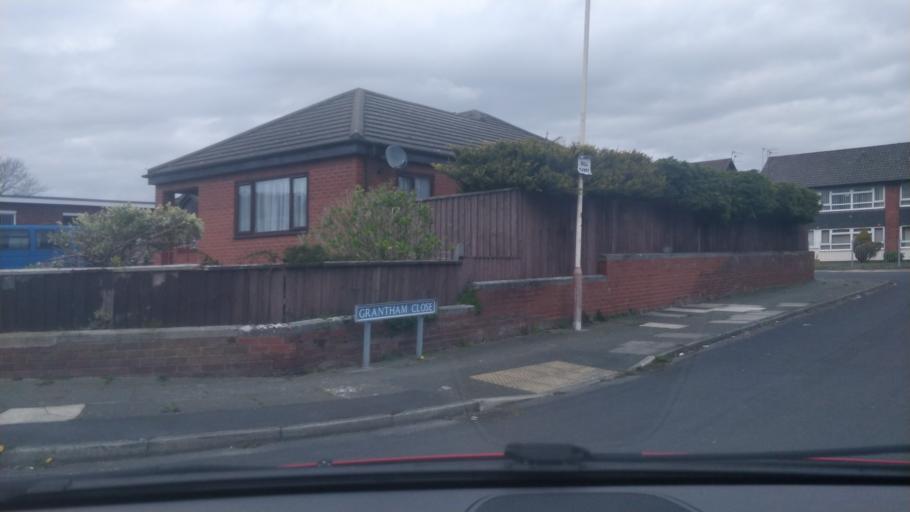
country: GB
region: England
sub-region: Sefton
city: Southport
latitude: 53.6183
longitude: -3.0112
